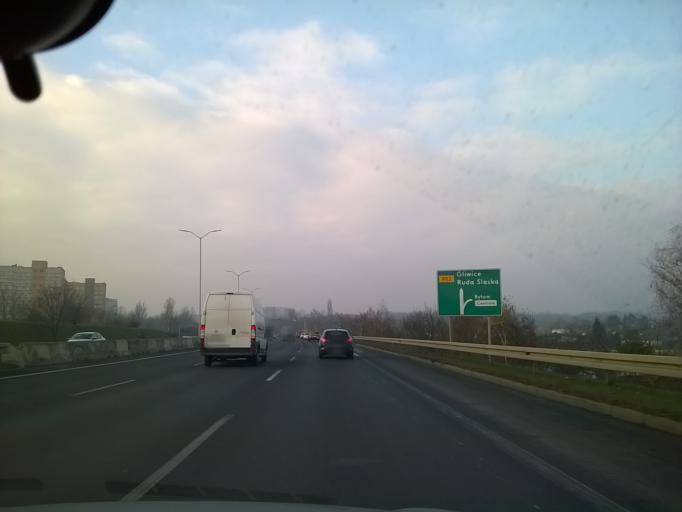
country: PL
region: Silesian Voivodeship
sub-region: Swietochlowice
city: Swietochlowice
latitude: 50.2935
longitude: 18.9272
